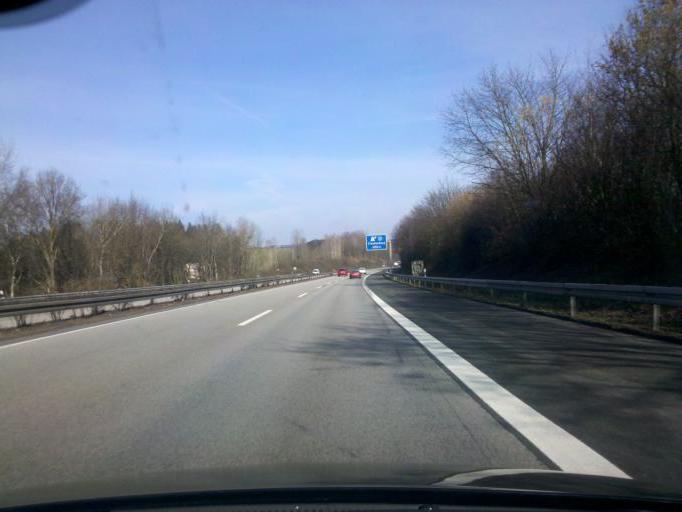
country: DE
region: North Rhine-Westphalia
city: Freudenberg
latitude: 50.8983
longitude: 7.9208
